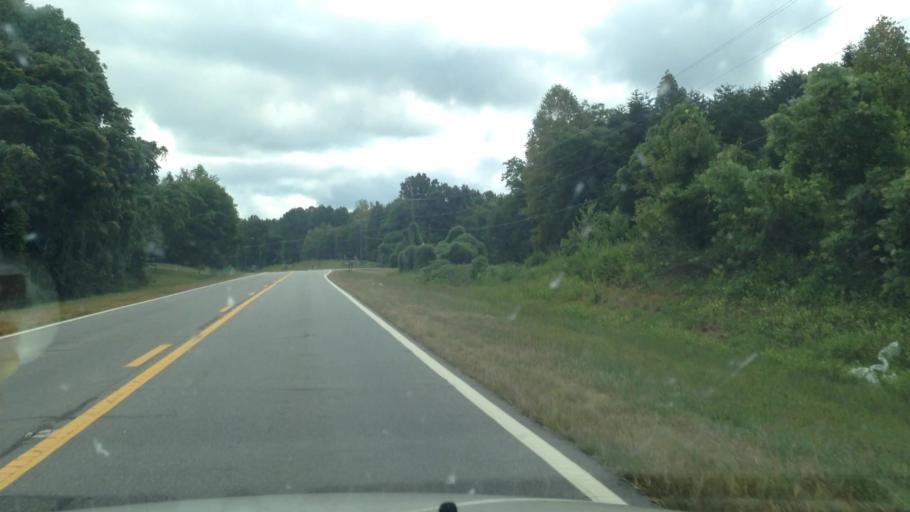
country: US
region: North Carolina
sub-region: Rockingham County
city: Wentworth
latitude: 36.3771
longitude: -79.8399
